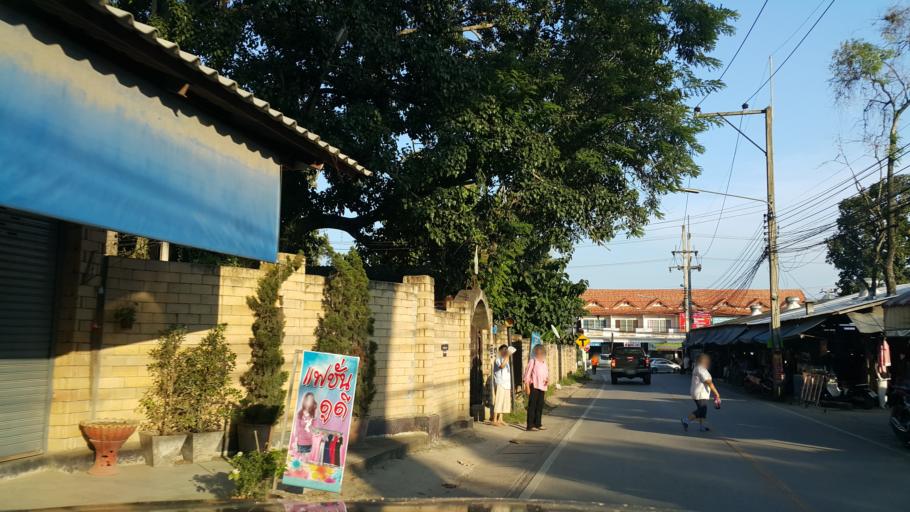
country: TH
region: Chiang Mai
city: San Sai
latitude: 18.9342
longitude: 98.9403
